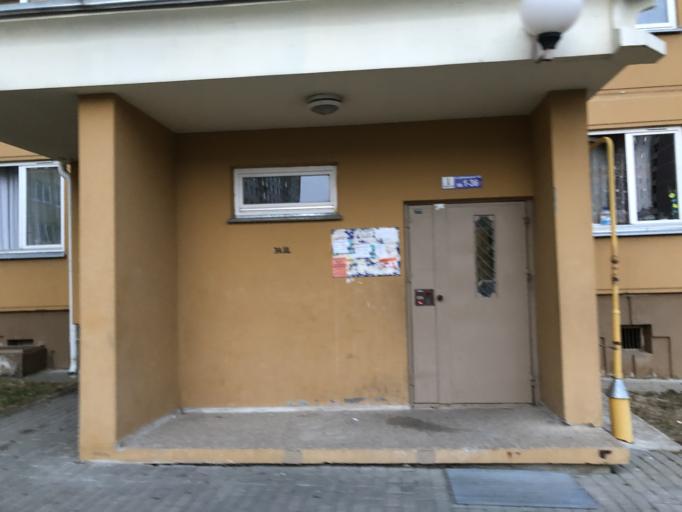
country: BY
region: Grodnenskaya
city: Hrodna
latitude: 53.6985
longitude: 23.8346
